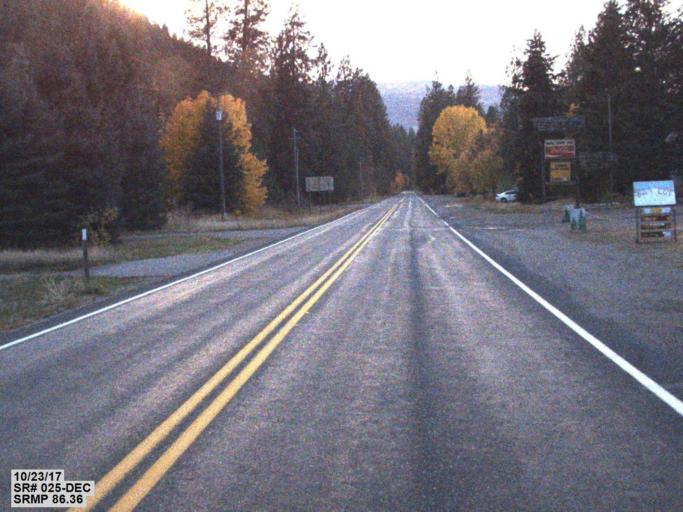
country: US
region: Washington
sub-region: Stevens County
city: Kettle Falls
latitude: 48.6642
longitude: -118.0588
